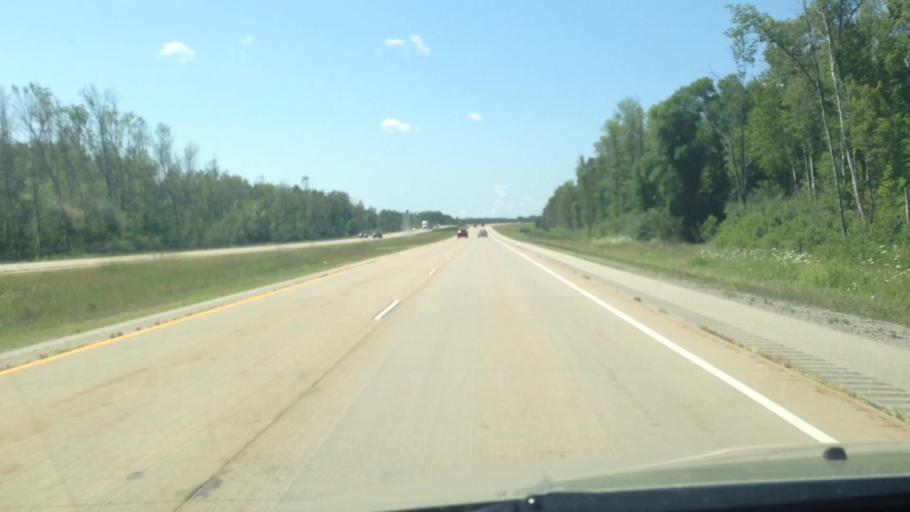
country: US
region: Wisconsin
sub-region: Oconto County
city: Oconto
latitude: 44.9147
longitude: -87.8772
